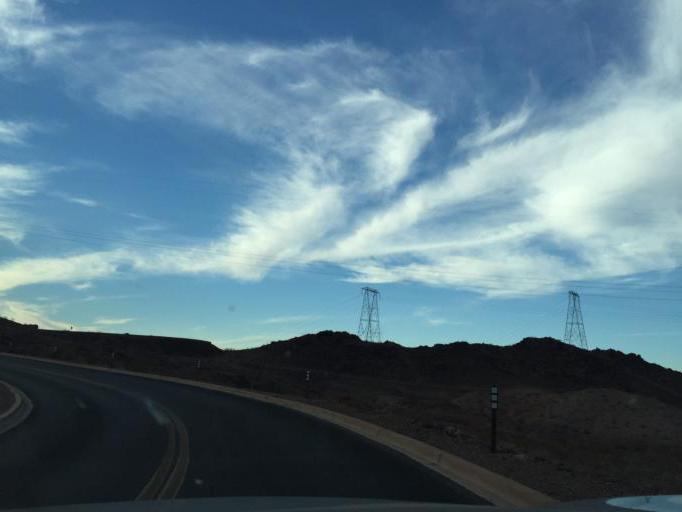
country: US
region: Nevada
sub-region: Clark County
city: Boulder City
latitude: 36.0154
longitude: -114.7599
